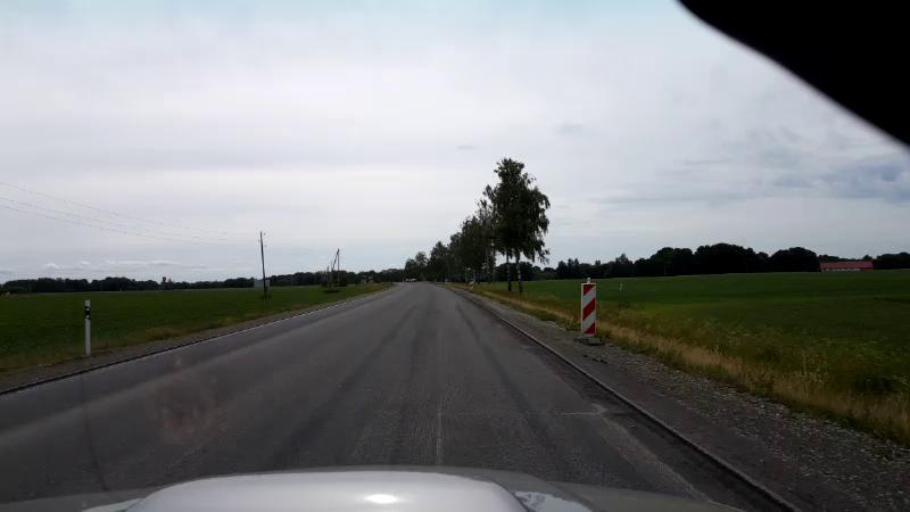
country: LV
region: Bauskas Rajons
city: Bauska
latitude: 56.3328
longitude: 24.2988
